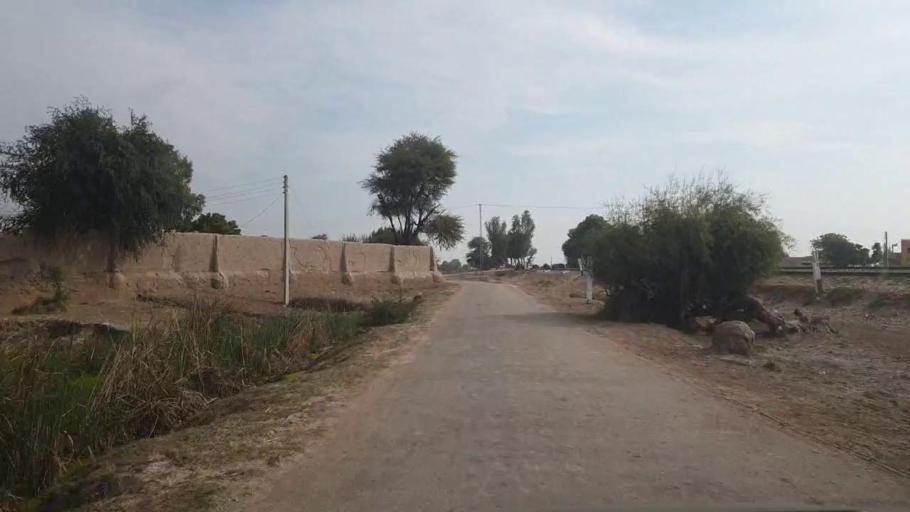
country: PK
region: Sindh
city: Shahpur Chakar
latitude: 26.0820
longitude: 68.4921
